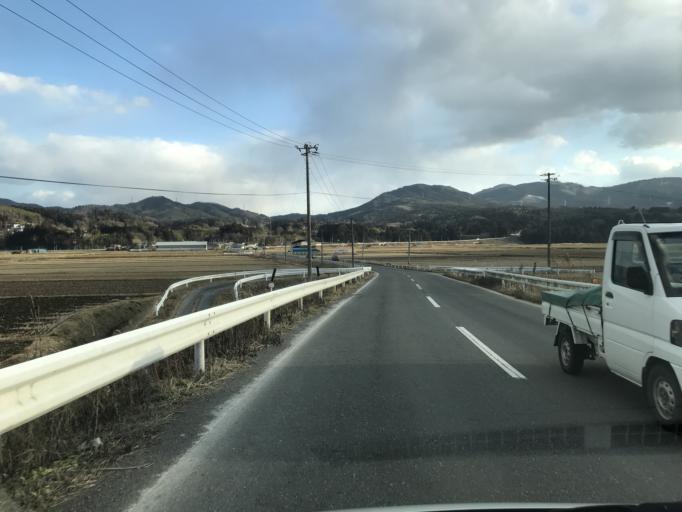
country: JP
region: Iwate
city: Mizusawa
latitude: 39.0631
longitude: 141.1678
